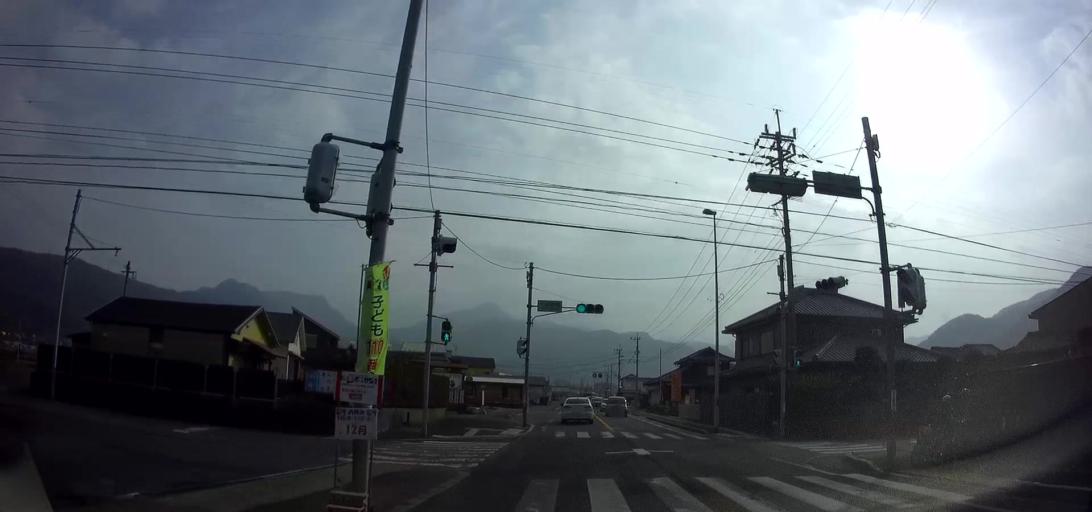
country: JP
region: Nagasaki
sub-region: Isahaya-shi
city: Isahaya
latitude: 32.7879
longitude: 130.1923
